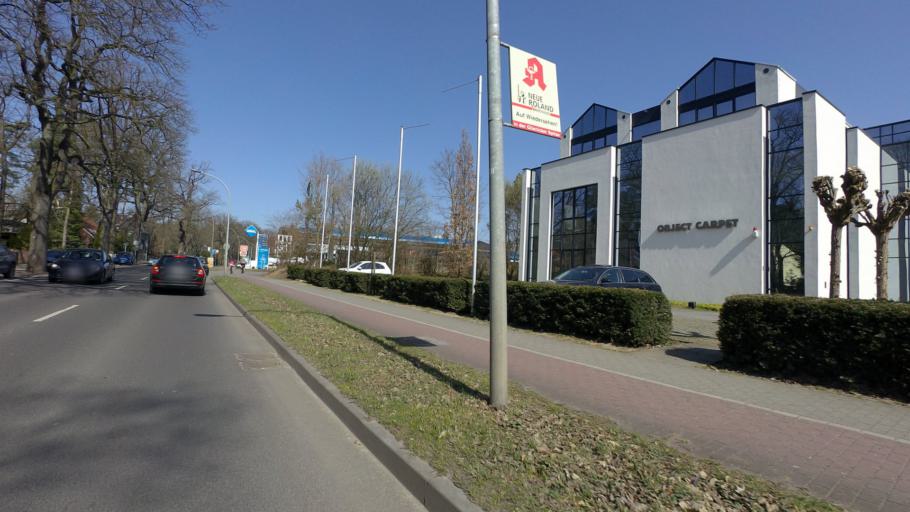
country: DE
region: Berlin
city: Frohnau
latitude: 52.6358
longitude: 13.3070
